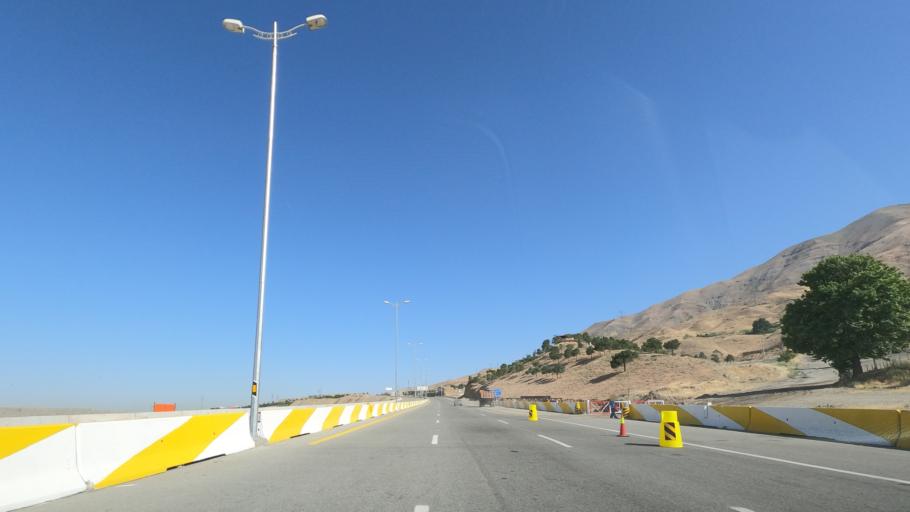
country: IR
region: Tehran
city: Shahr-e Qods
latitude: 35.7591
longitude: 51.0769
